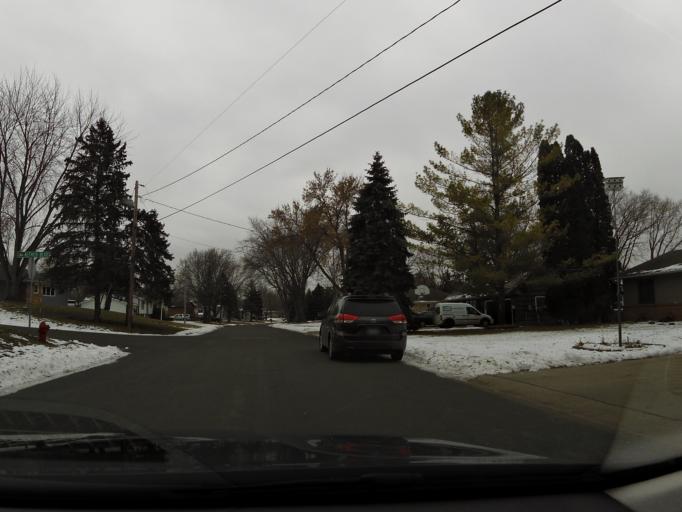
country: US
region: Minnesota
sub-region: Carver County
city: Waconia
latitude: 44.8605
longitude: -93.7989
